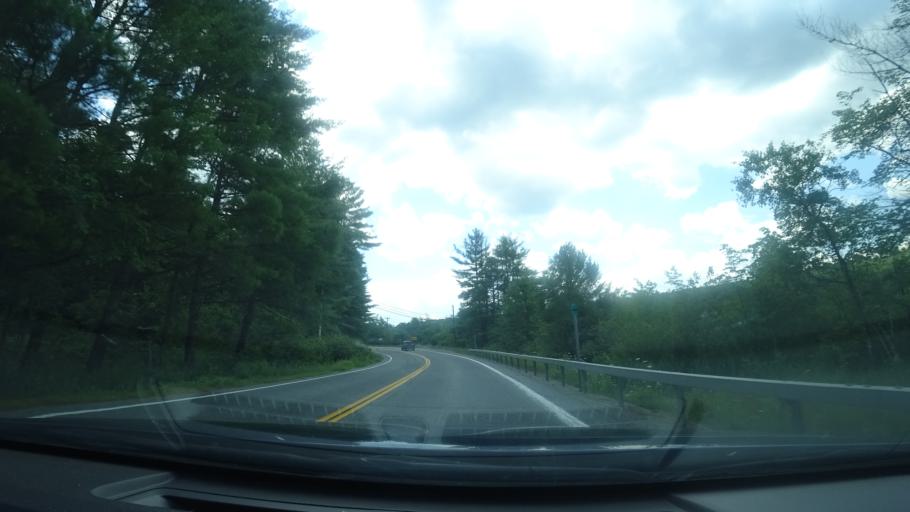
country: US
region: New York
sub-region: Warren County
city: Warrensburg
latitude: 43.6623
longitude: -73.8212
